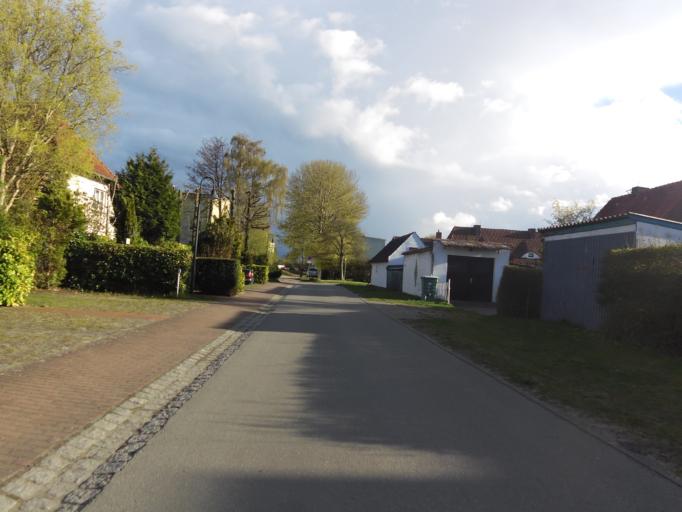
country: DE
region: Mecklenburg-Vorpommern
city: Zingst
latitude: 54.4360
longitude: 12.6939
